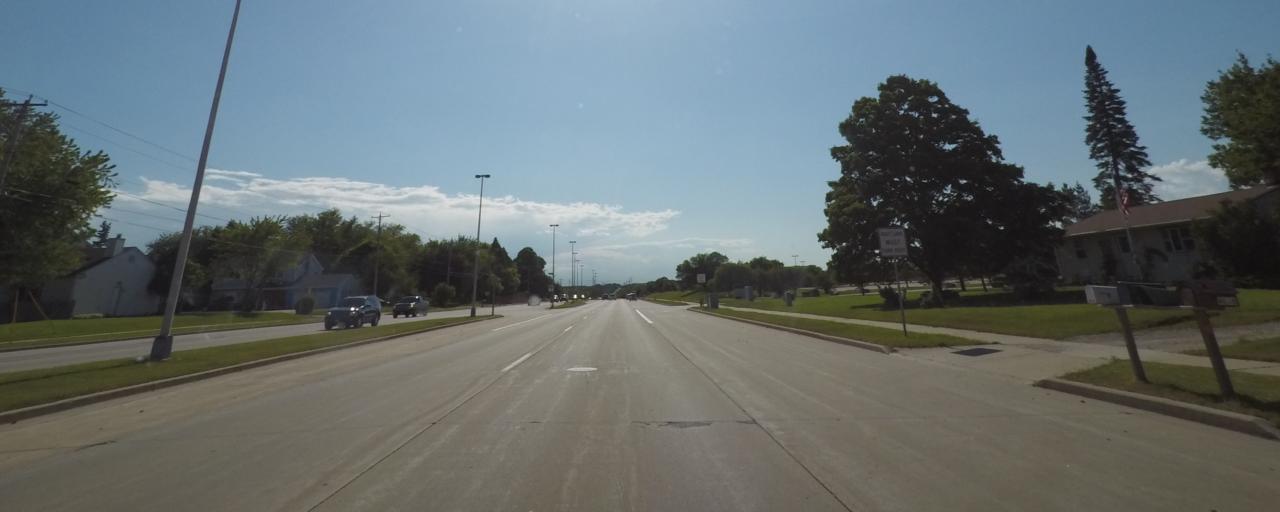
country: US
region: Wisconsin
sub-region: Milwaukee County
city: Greendale
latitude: 42.9162
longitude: -87.9740
